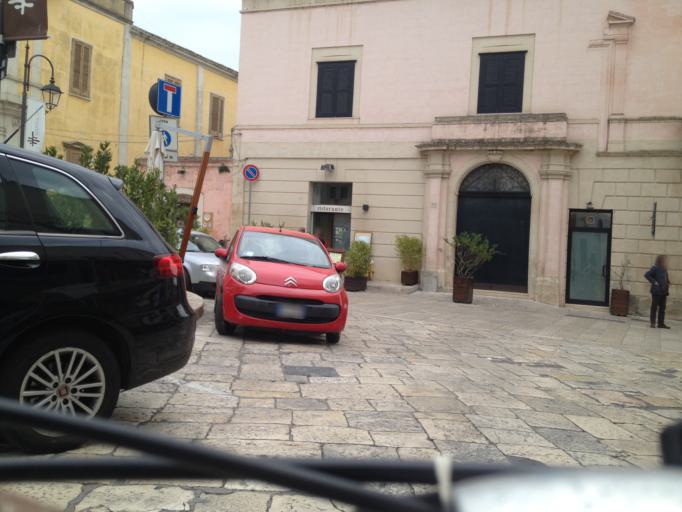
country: IT
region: Basilicate
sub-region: Provincia di Matera
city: Matera
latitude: 40.6649
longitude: 16.6088
